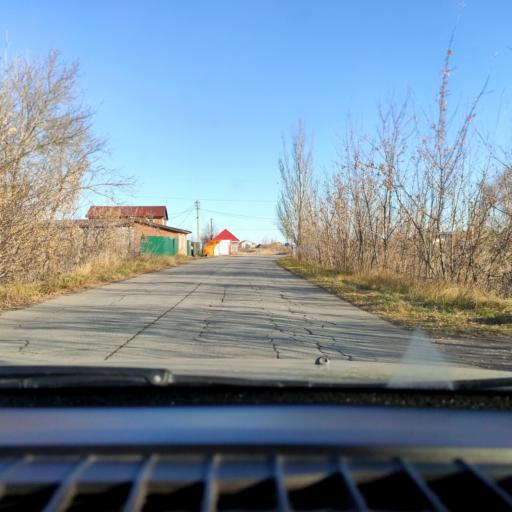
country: RU
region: Samara
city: Tol'yatti
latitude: 53.6637
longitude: 49.3363
